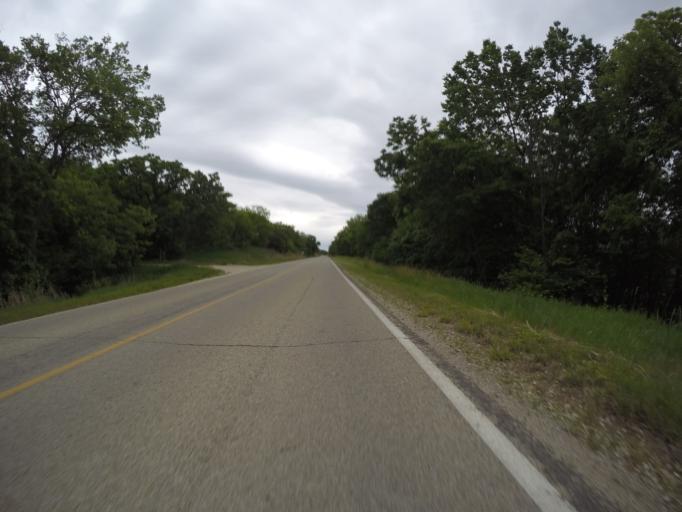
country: US
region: Kansas
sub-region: Pottawatomie County
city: Wamego
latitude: 39.1825
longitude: -96.3655
